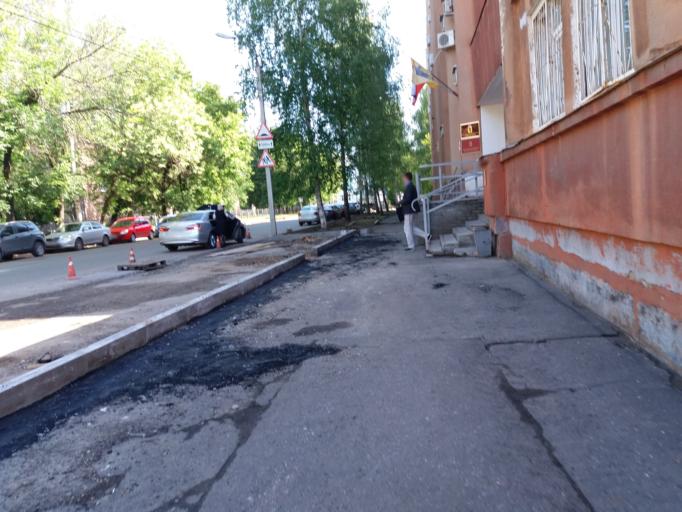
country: RU
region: Jaroslavl
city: Yaroslavl
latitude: 57.6395
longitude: 39.8520
